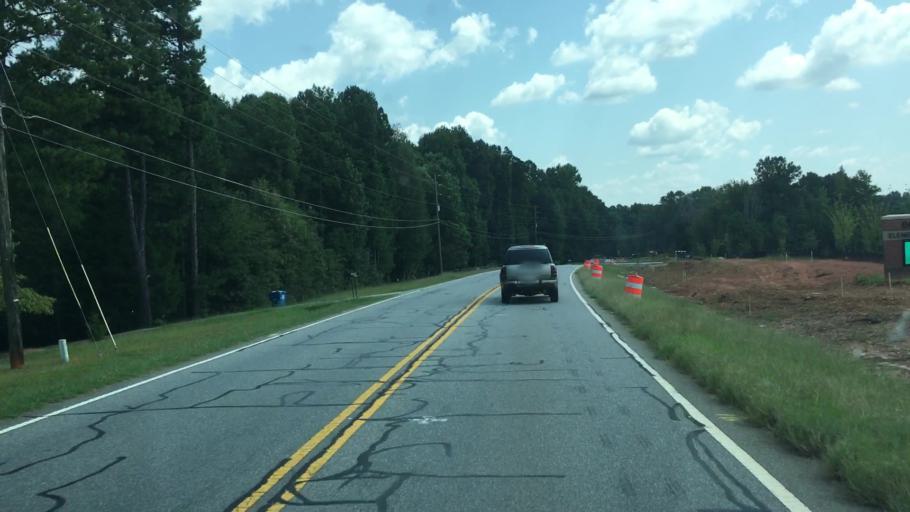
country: US
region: Georgia
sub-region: Barrow County
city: Statham
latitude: 33.9195
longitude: -83.6068
